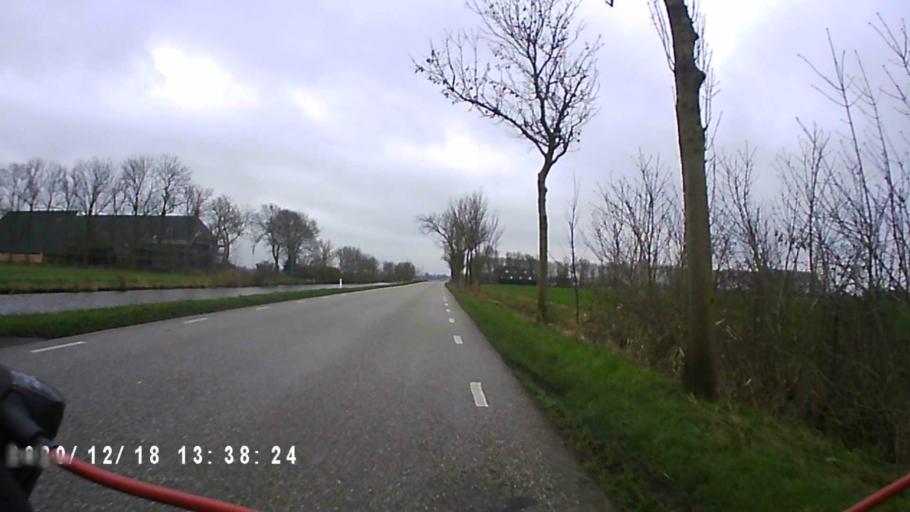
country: NL
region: Groningen
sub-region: Gemeente Bedum
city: Bedum
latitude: 53.3302
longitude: 6.5924
